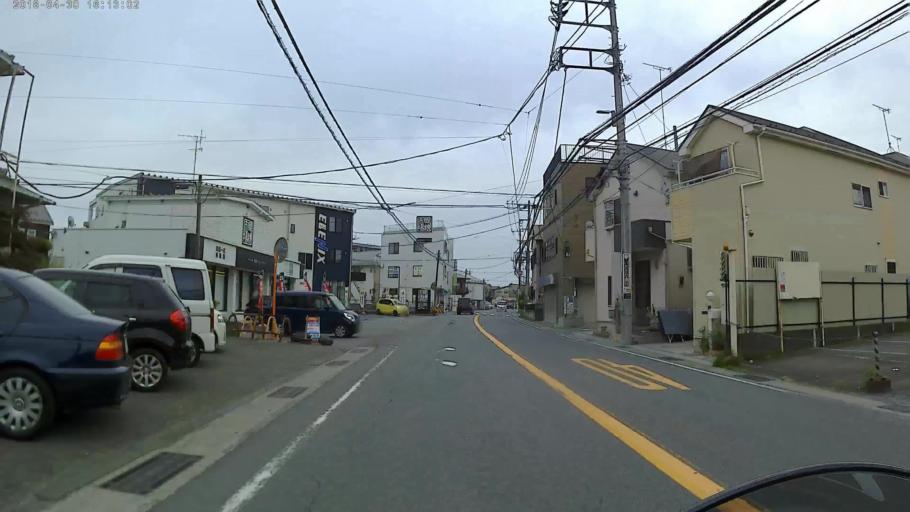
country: JP
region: Kanagawa
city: Minami-rinkan
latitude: 35.4922
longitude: 139.4311
